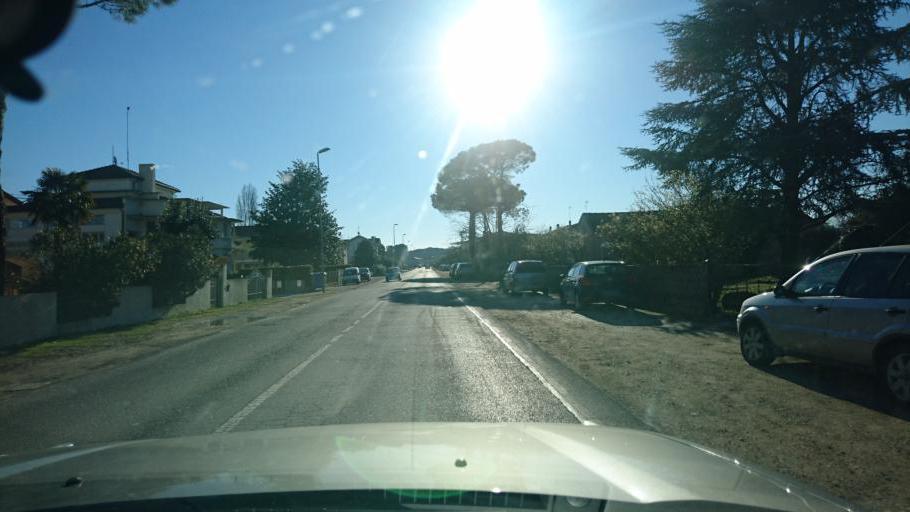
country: IT
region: Veneto
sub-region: Provincia di Rovigo
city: Porto Viro
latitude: 45.0441
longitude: 12.2153
